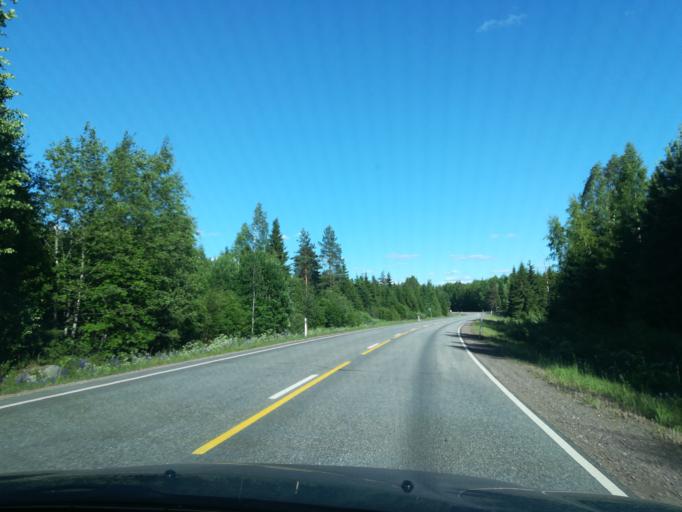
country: FI
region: South Karelia
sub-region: Imatra
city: Ruokolahti
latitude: 61.3524
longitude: 28.7317
